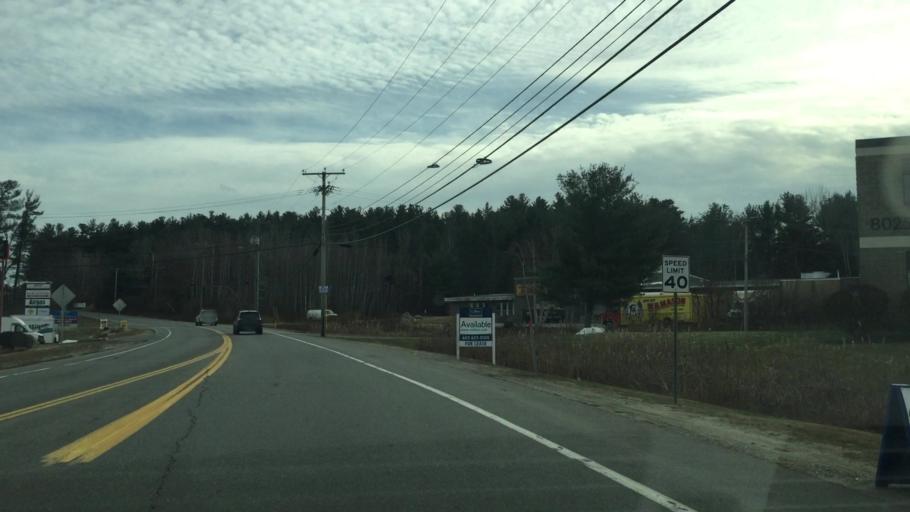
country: US
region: New Hampshire
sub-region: Hillsborough County
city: Manchester
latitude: 42.9416
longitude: -71.4262
